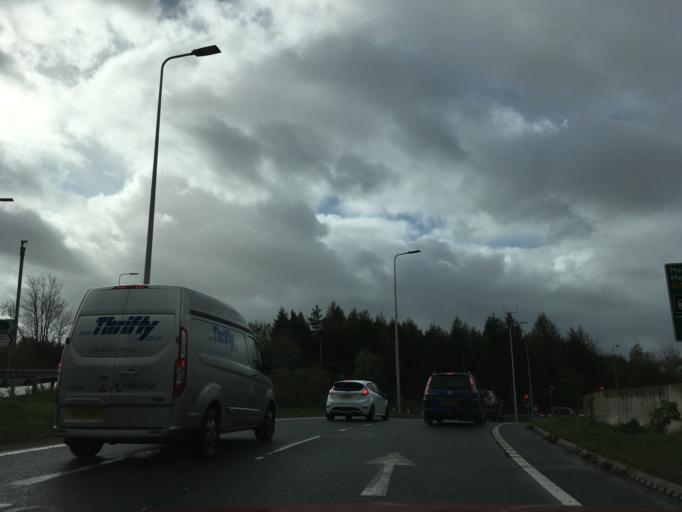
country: GB
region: Wales
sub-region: Cardiff
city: Radyr
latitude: 51.5272
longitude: -3.2372
